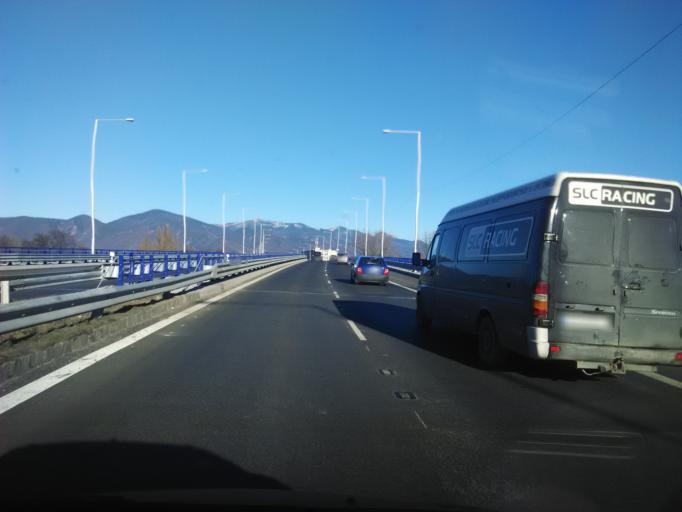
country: SK
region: Zilinsky
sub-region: Okres Martin
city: Martin
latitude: 49.0692
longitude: 18.9128
